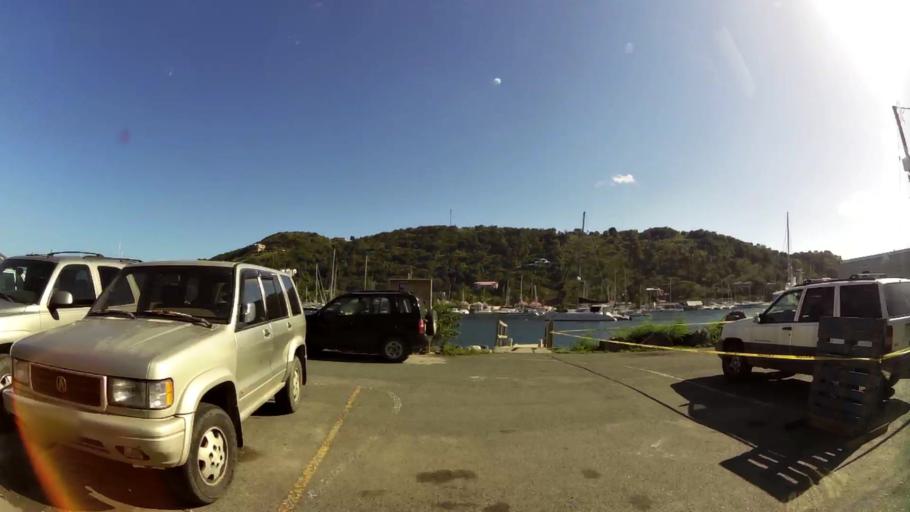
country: VG
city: Road Town
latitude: 18.3879
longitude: -64.7030
